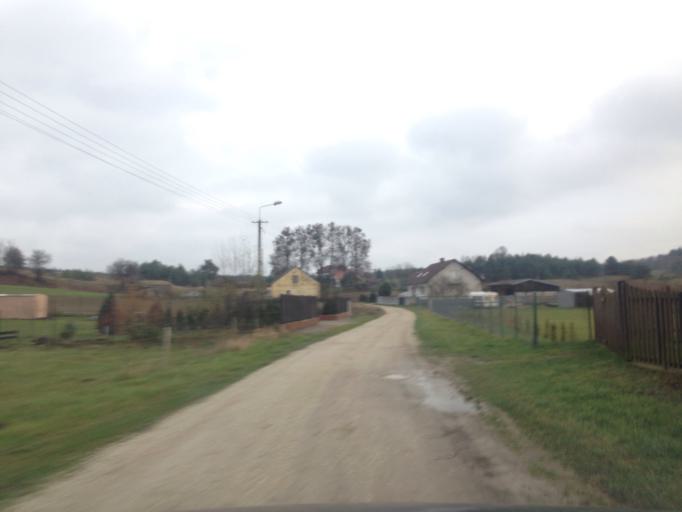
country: PL
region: Kujawsko-Pomorskie
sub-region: Powiat brodnicki
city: Gorzno
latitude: 53.2107
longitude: 19.6679
